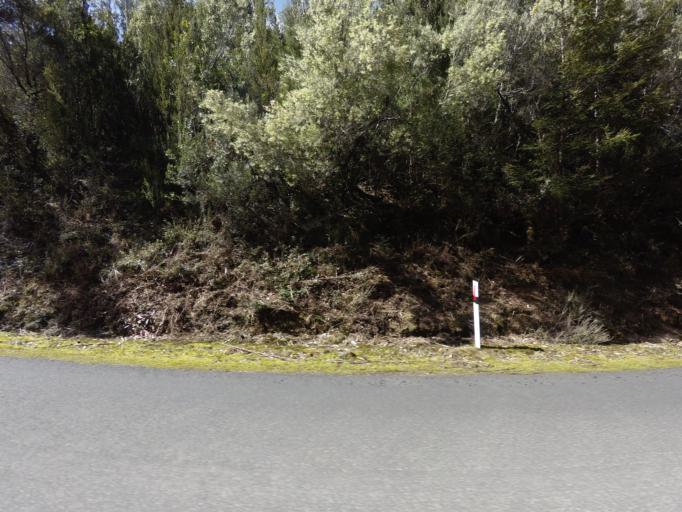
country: AU
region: Tasmania
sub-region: Derwent Valley
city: New Norfolk
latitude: -42.7243
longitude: 146.4349
